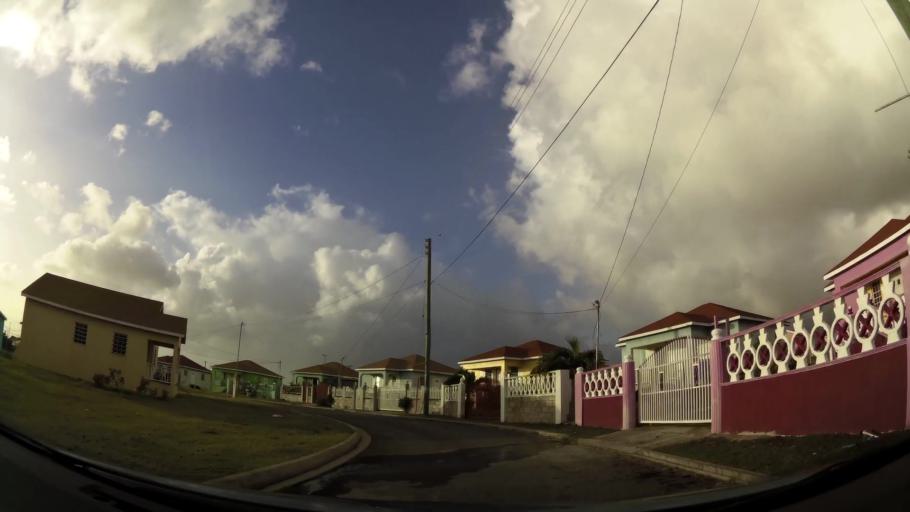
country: KN
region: Saint John Figtree
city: Fig Tree
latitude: 17.1181
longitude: -62.6137
